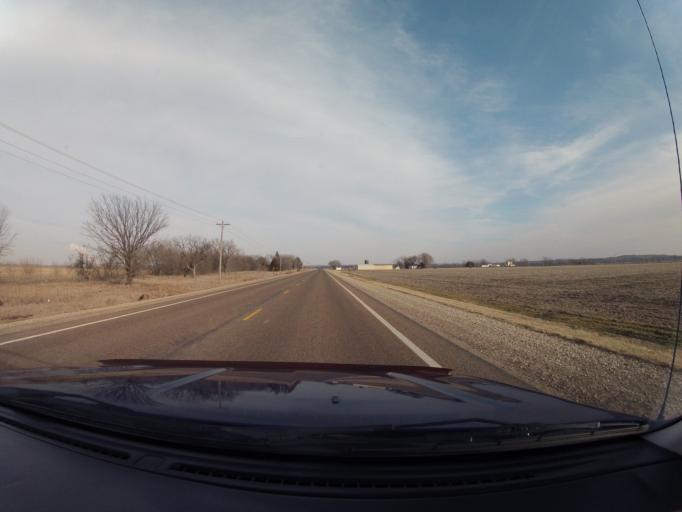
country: US
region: Kansas
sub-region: Pottawatomie County
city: Wamego
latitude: 39.2096
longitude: -96.2732
